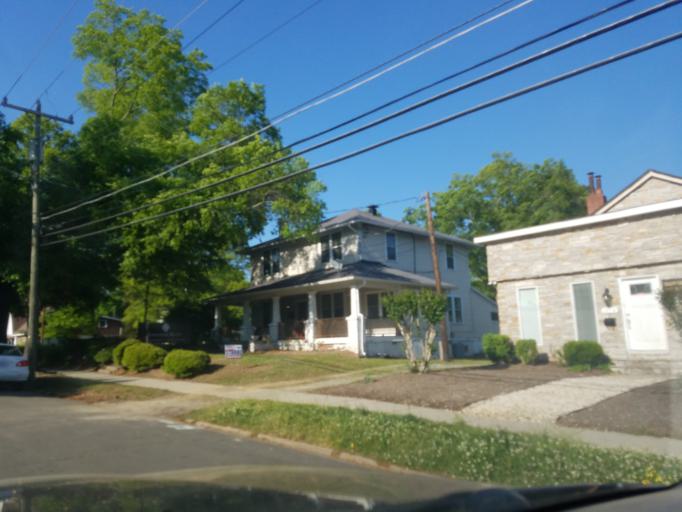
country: US
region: North Carolina
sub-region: Durham County
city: Durham
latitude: 36.0147
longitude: -78.9193
